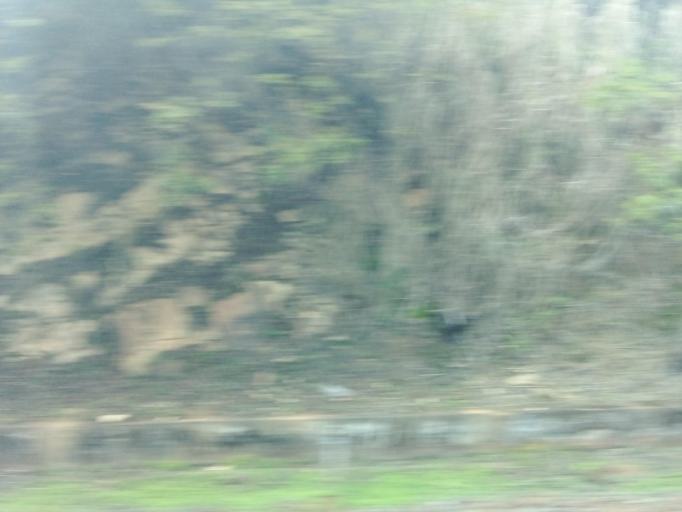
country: BR
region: Minas Gerais
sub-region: Governador Valadares
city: Governador Valadares
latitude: -18.9249
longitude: -42.0176
